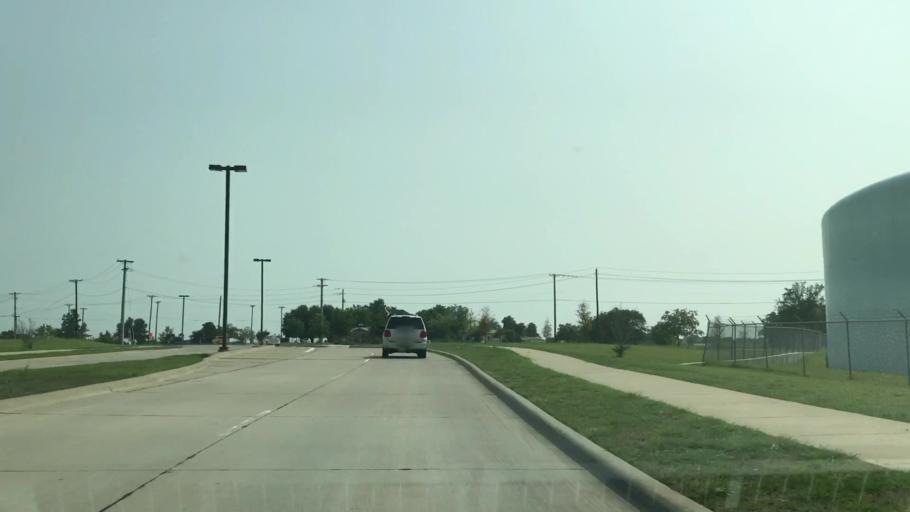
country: US
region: Texas
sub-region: Dallas County
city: Rowlett
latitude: 32.9436
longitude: -96.5695
